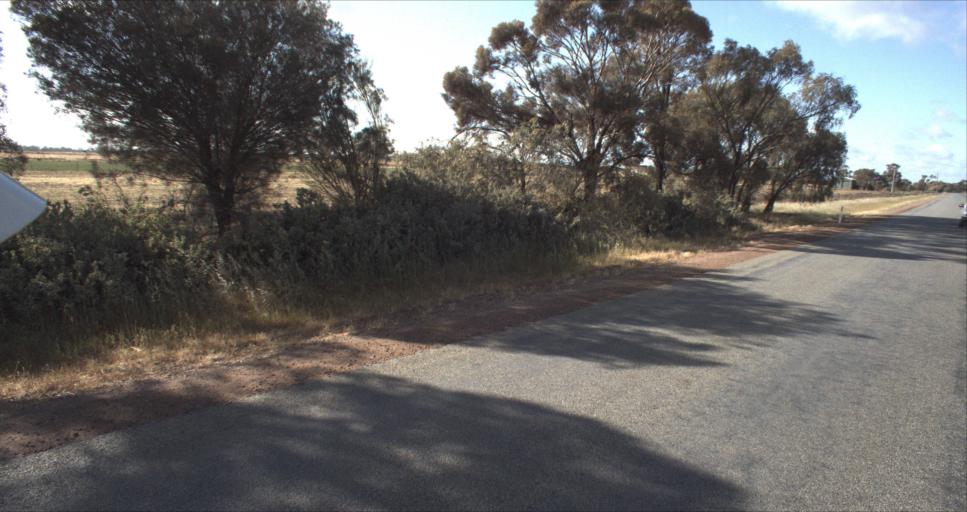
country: AU
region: New South Wales
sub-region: Leeton
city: Leeton
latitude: -34.5087
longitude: 146.3926
